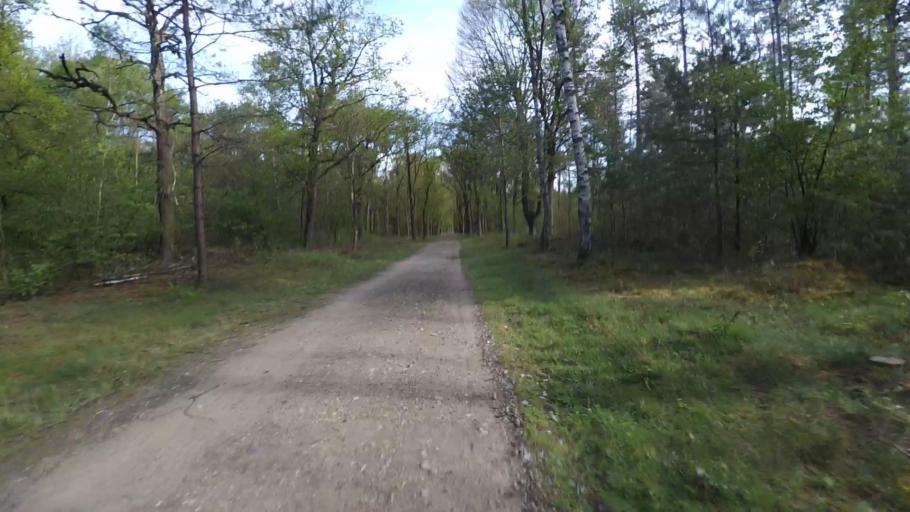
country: NL
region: Utrecht
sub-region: Gemeente Utrechtse Heuvelrug
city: Driebergen-Rijsenburg
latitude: 52.0959
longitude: 5.3083
